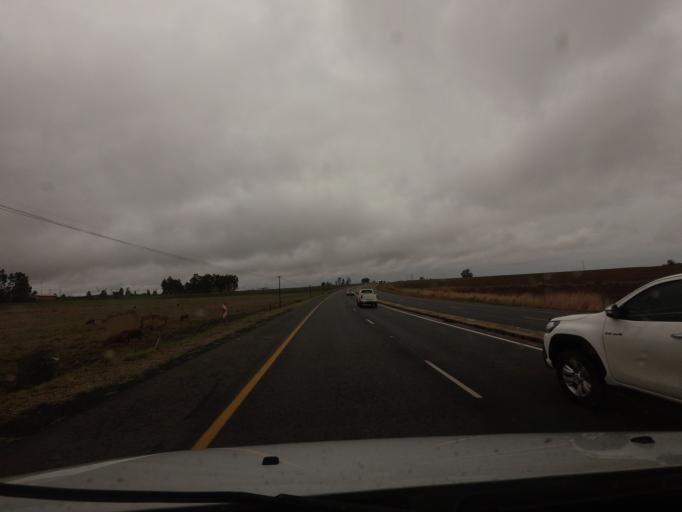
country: ZA
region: Mpumalanga
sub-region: Nkangala District Municipality
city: Belfast
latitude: -25.7655
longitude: 29.9603
